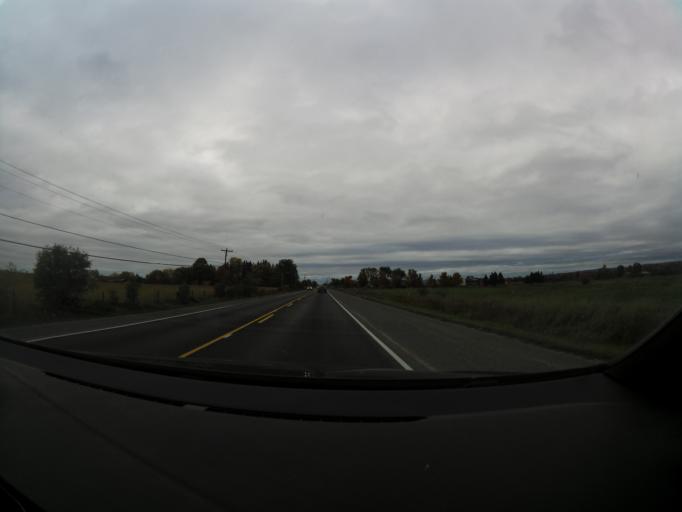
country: CA
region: Ontario
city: Bells Corners
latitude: 45.4309
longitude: -76.0321
